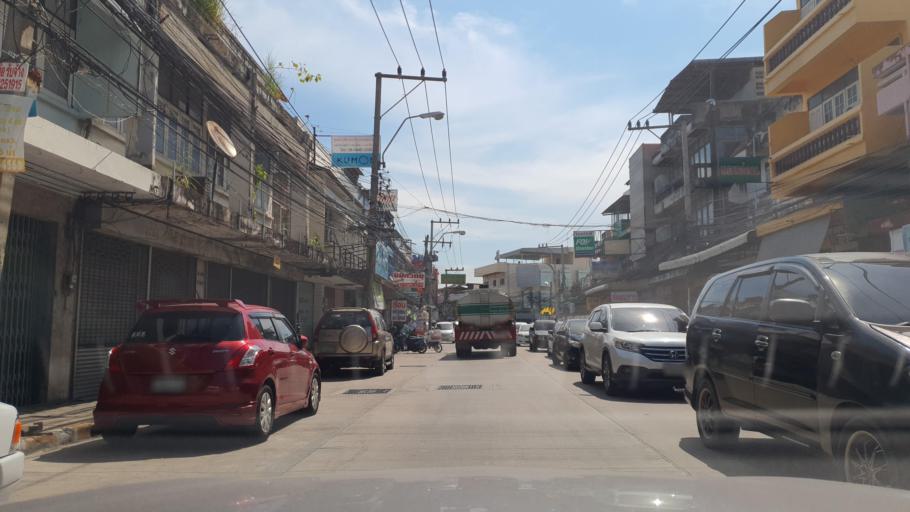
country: TH
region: Chon Buri
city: Phatthaya
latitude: 12.9712
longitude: 100.9055
